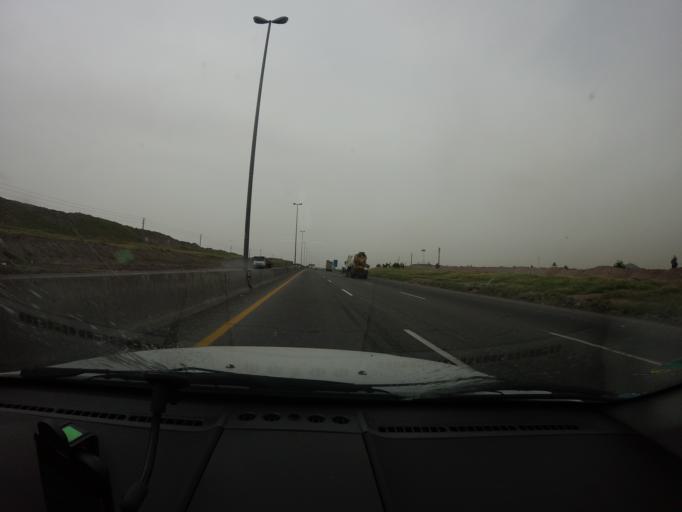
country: IR
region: Tehran
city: Robat Karim
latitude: 35.4799
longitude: 51.0430
